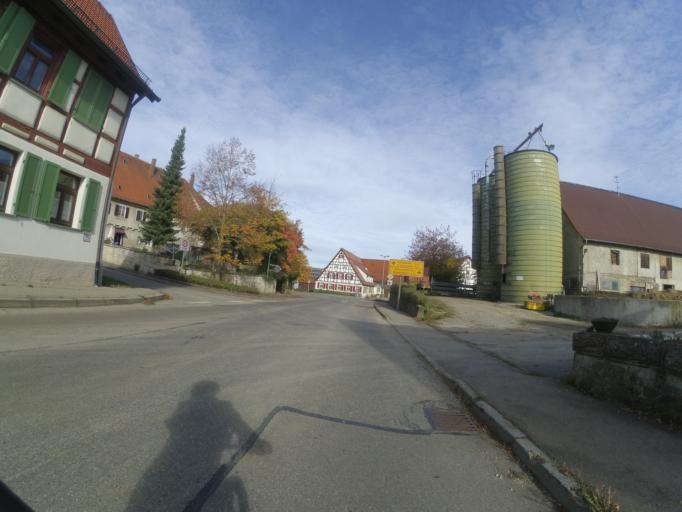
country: DE
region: Baden-Wuerttemberg
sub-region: Tuebingen Region
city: Amstetten
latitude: 48.5943
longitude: 9.9176
